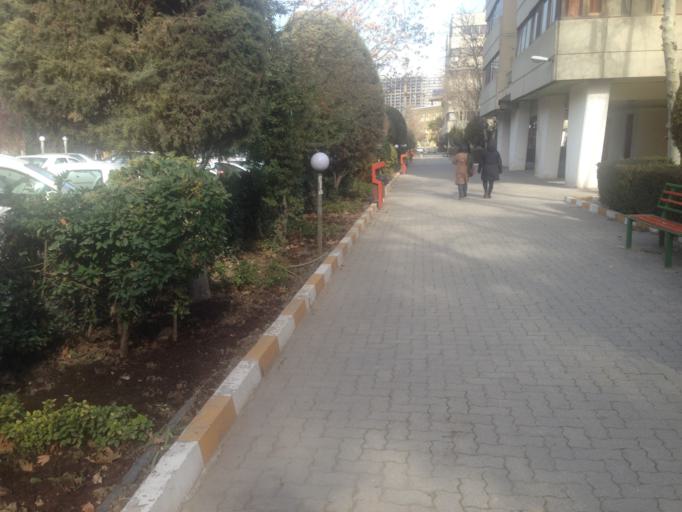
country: IR
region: Tehran
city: Tehran
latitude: 35.7126
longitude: 51.3107
